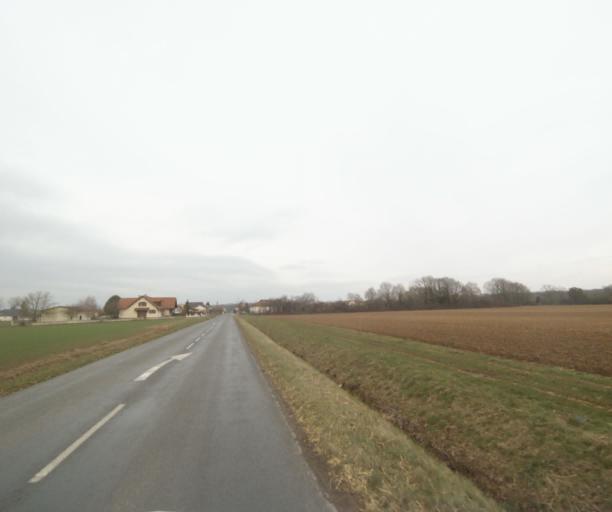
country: FR
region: Champagne-Ardenne
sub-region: Departement de la Haute-Marne
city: Villiers-en-Lieu
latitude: 48.6777
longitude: 4.8867
